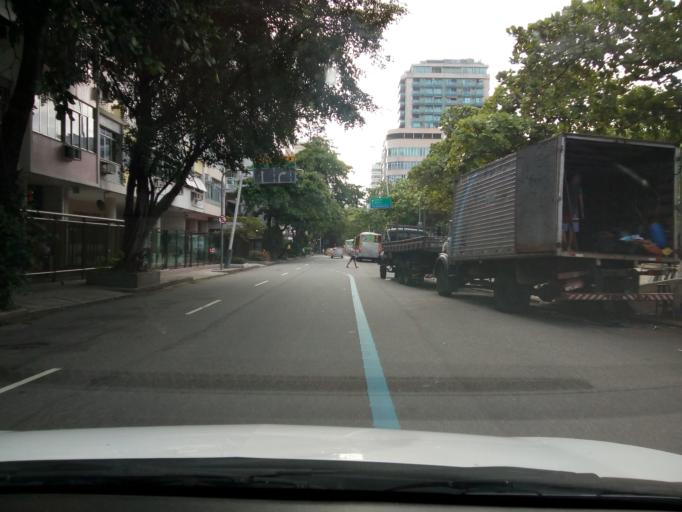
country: BR
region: Rio de Janeiro
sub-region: Rio De Janeiro
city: Rio de Janeiro
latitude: -22.9857
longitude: -43.1972
